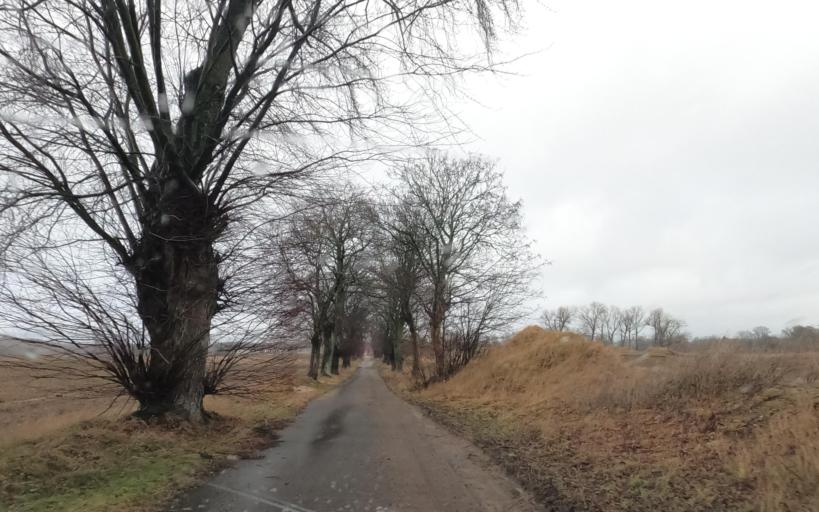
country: PL
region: West Pomeranian Voivodeship
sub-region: Powiat szczecinecki
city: Szczecinek
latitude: 53.6260
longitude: 16.6761
